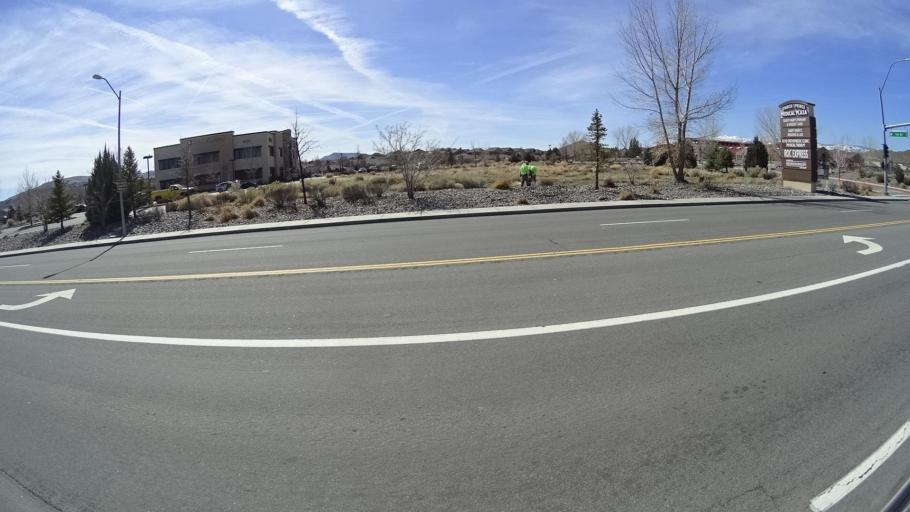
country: US
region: Nevada
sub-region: Washoe County
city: Sun Valley
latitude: 39.5854
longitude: -119.7313
